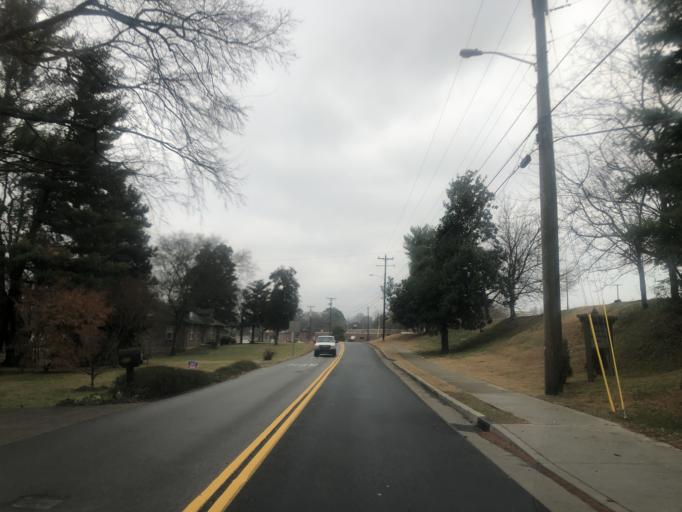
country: US
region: Tennessee
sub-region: Davidson County
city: Lakewood
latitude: 36.1716
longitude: -86.6824
